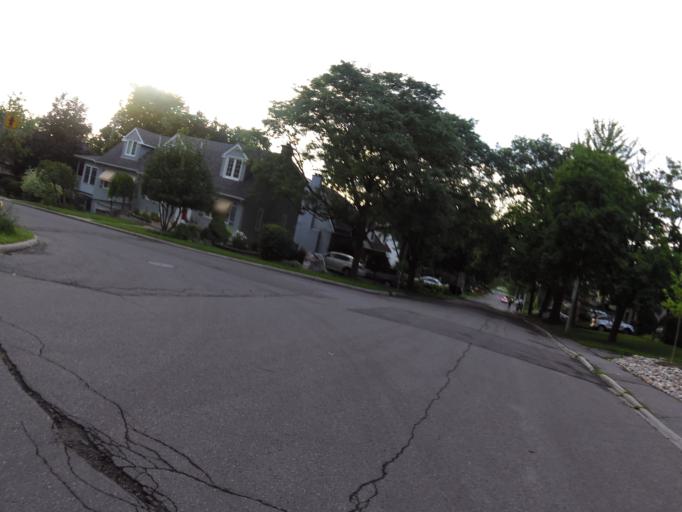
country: CA
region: Ontario
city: Ottawa
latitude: 45.3844
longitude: -75.7608
